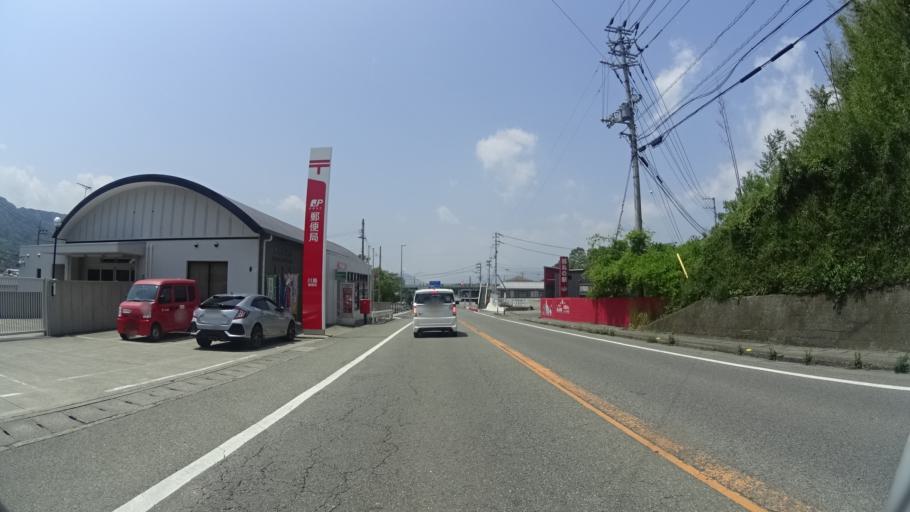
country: JP
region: Tokushima
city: Kamojimacho-jogejima
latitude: 34.0650
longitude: 134.3213
